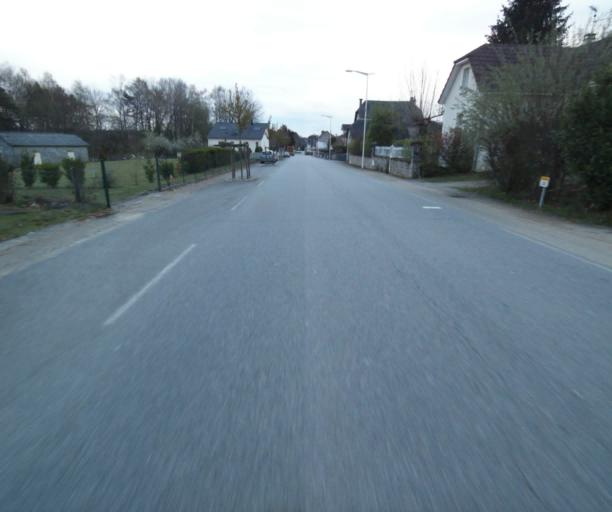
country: FR
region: Limousin
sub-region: Departement de la Correze
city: Correze
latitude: 45.3338
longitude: 1.8783
